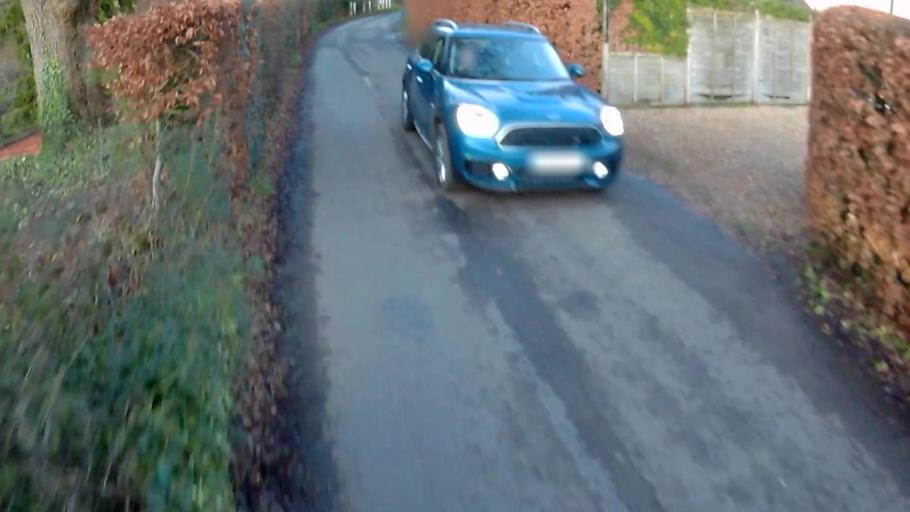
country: GB
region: England
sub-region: Hampshire
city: Overton
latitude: 51.2306
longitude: -1.2186
